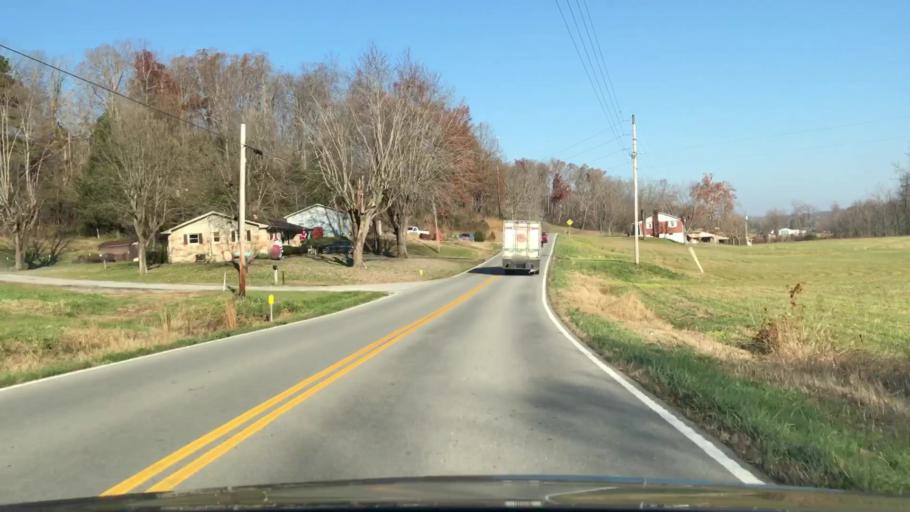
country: US
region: Kentucky
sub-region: Grayson County
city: Leitchfield
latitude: 37.4473
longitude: -86.2901
